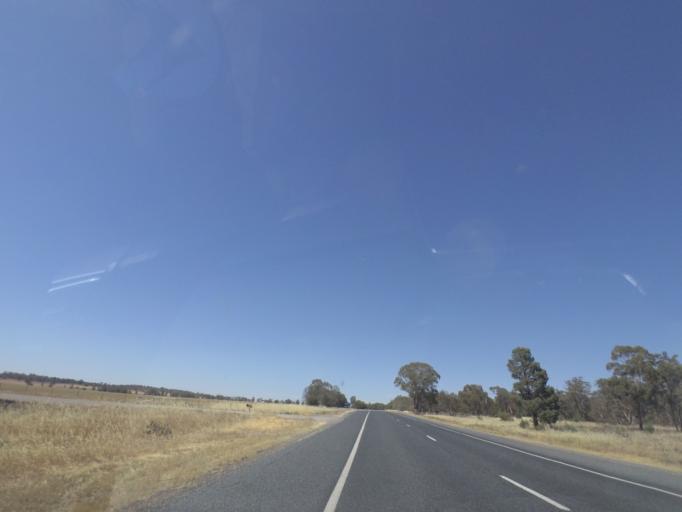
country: AU
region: New South Wales
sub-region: Narrandera
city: Narrandera
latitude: -34.4453
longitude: 146.8400
